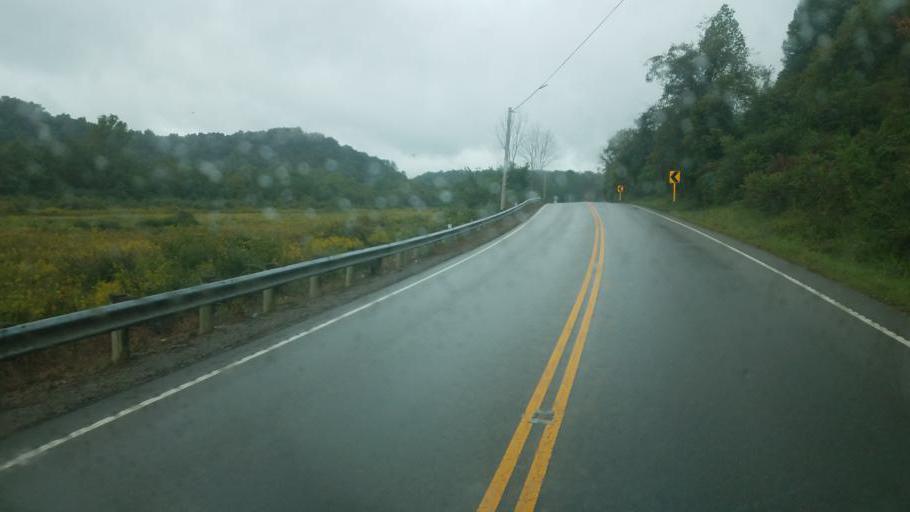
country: US
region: Ohio
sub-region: Jackson County
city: Oak Hill
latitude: 38.8226
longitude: -82.6676
